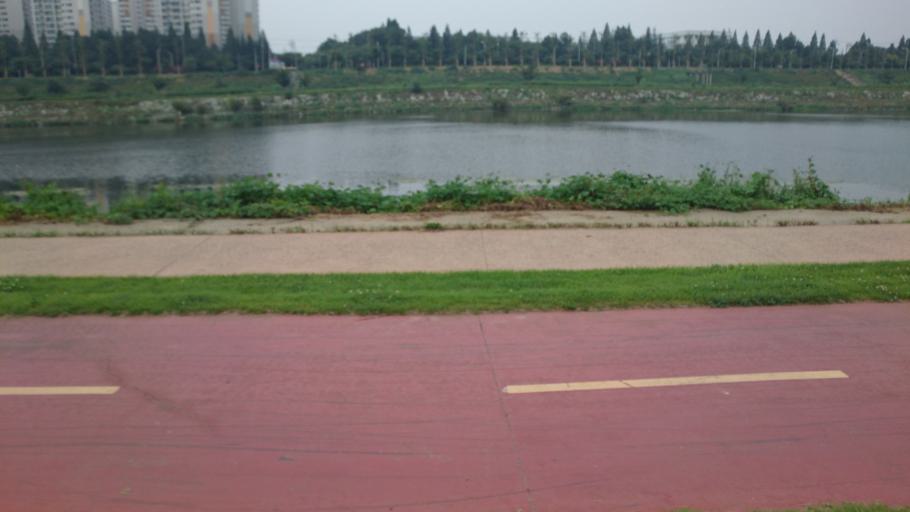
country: KR
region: Daegu
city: Hwawon
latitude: 35.8500
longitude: 128.4701
